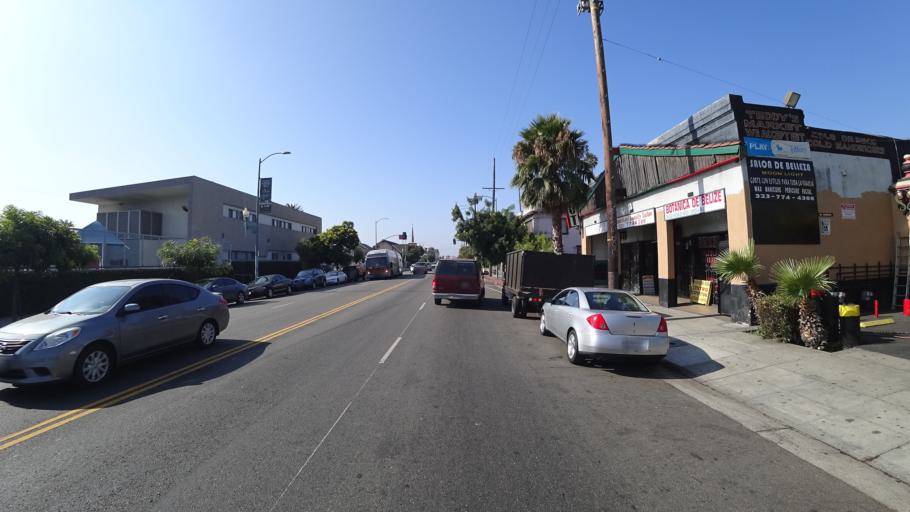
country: US
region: California
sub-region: Los Angeles County
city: Westmont
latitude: 33.9921
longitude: -118.2916
